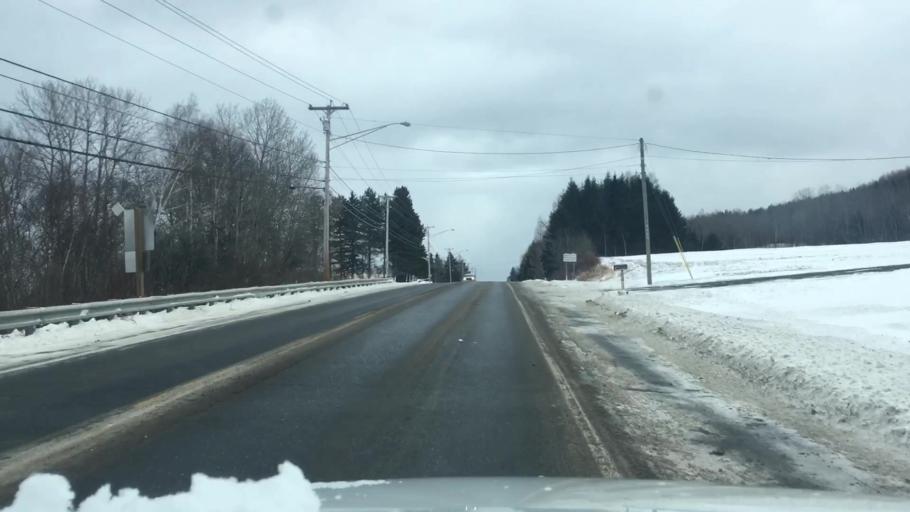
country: US
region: Maine
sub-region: Aroostook County
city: Madawaska
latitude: 47.3520
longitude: -68.2943
